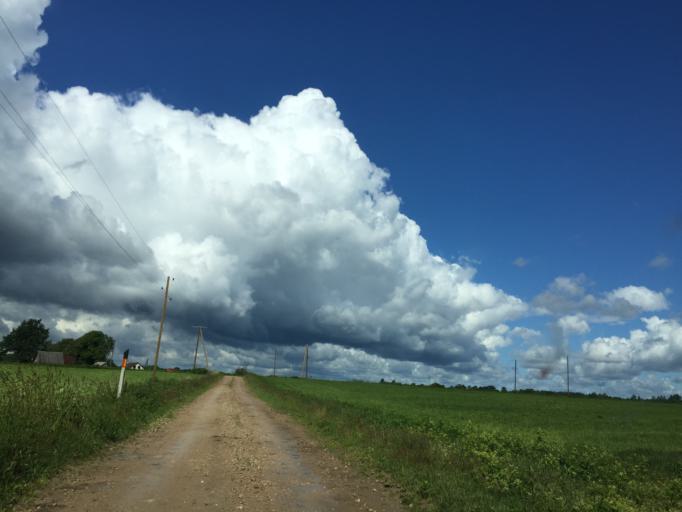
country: LV
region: Lecava
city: Iecava
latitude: 56.6166
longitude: 24.2064
